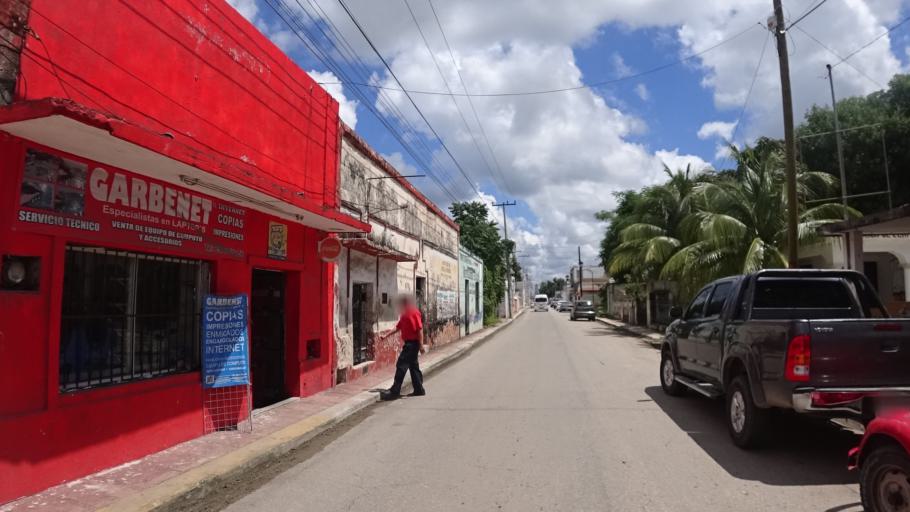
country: MX
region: Yucatan
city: Valladolid
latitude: 20.6900
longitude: -88.2115
